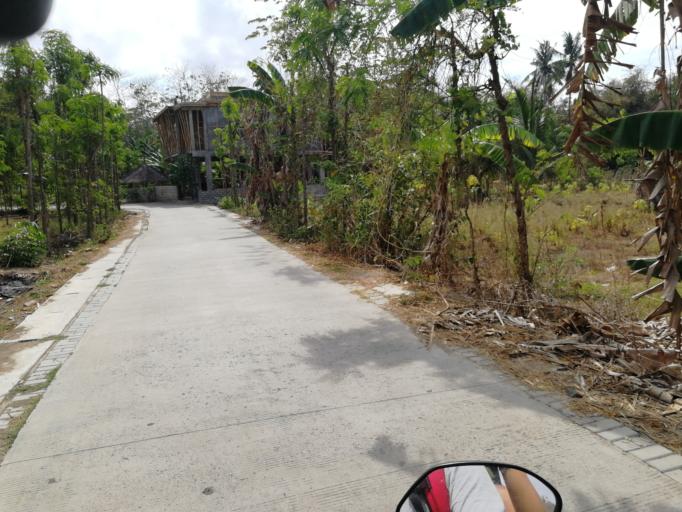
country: ID
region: West Nusa Tenggara
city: Kute
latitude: -8.8838
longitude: 116.2710
